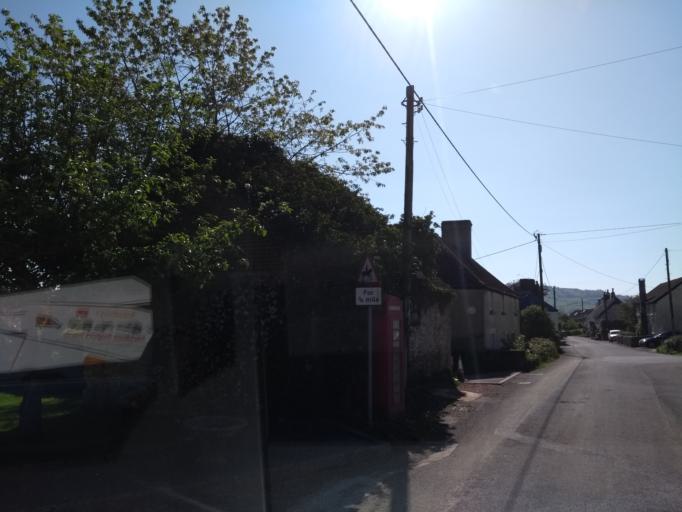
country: GB
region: England
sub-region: Devon
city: Colyton
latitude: 50.7556
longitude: -3.0515
